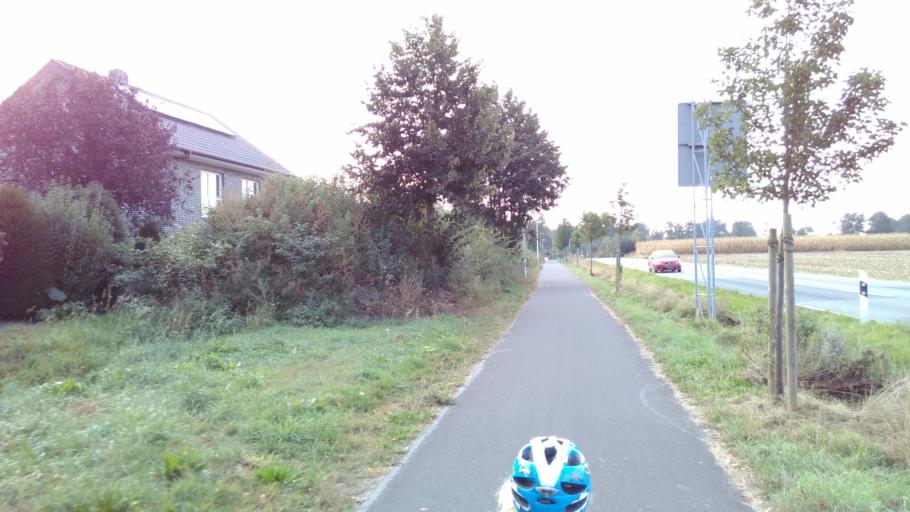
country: DE
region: North Rhine-Westphalia
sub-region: Regierungsbezirk Detmold
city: Verl
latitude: 51.8724
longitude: 8.4937
